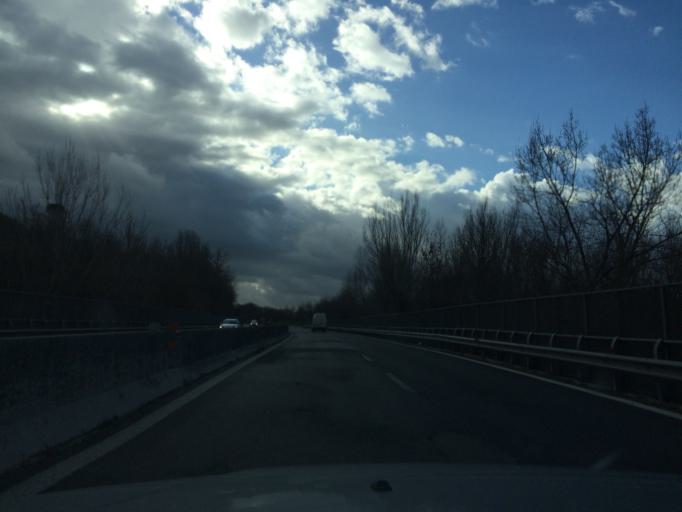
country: IT
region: Umbria
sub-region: Provincia di Terni
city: Acquasparta
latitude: 42.7127
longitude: 12.5518
